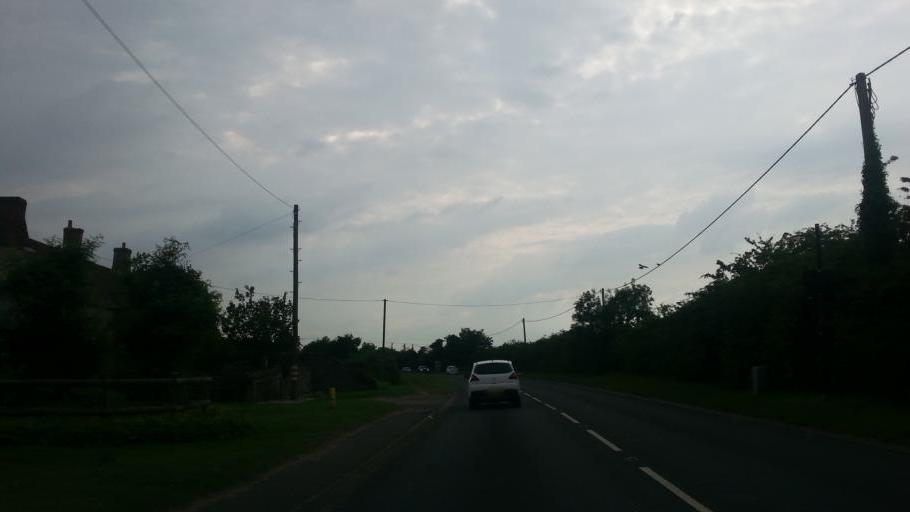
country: GB
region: England
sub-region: Norfolk
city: Dersingham
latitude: 52.7999
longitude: 0.5425
